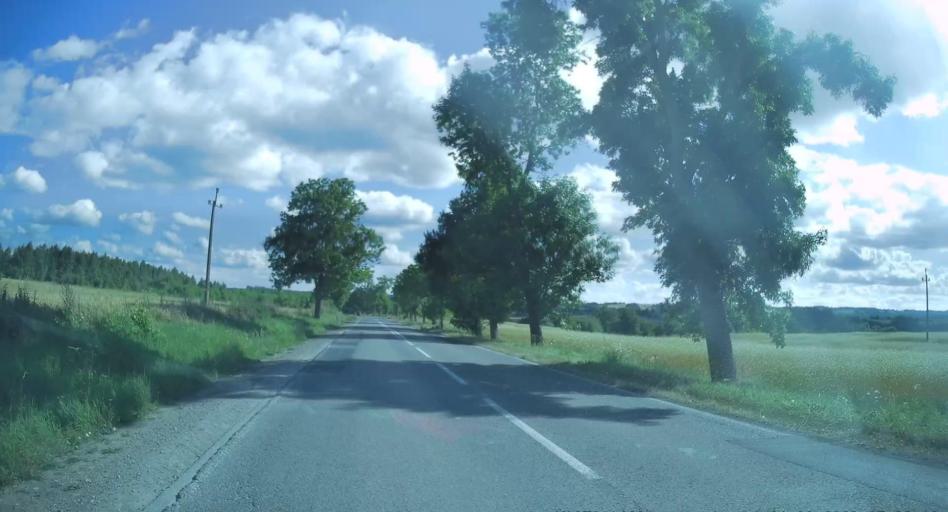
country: PL
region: Swietokrzyskie
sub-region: Powiat kielecki
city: Lagow
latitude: 50.7868
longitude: 21.0816
